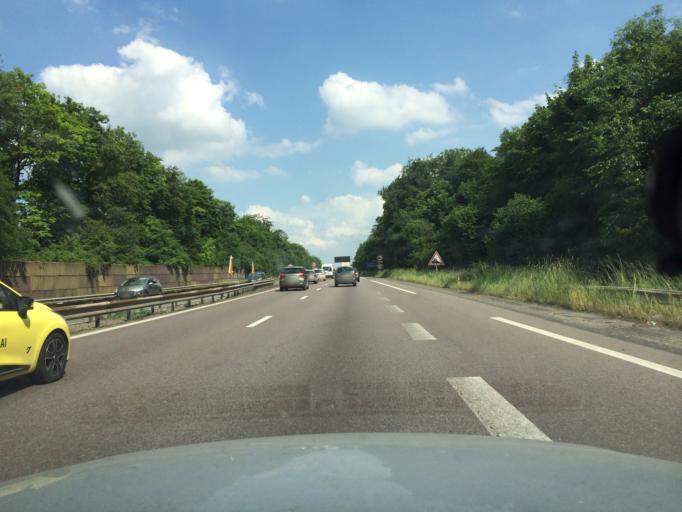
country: FR
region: Lorraine
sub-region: Departement de Meurthe-et-Moselle
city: Chavigny
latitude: 48.6451
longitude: 6.1453
